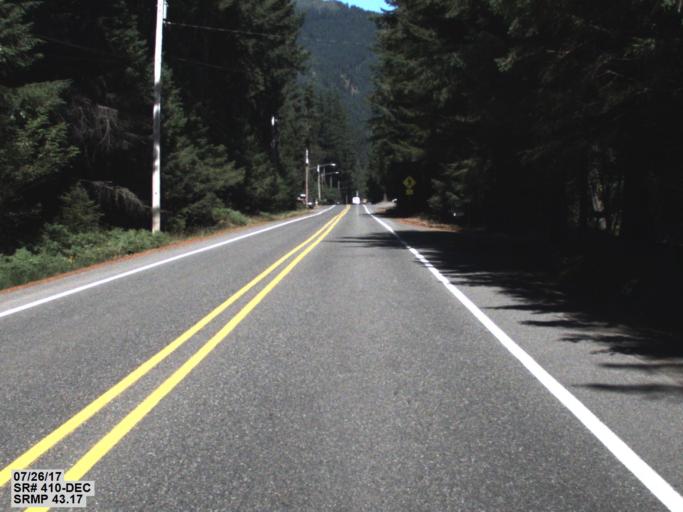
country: US
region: Washington
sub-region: King County
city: Riverbend
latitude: 47.1543
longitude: -121.6522
